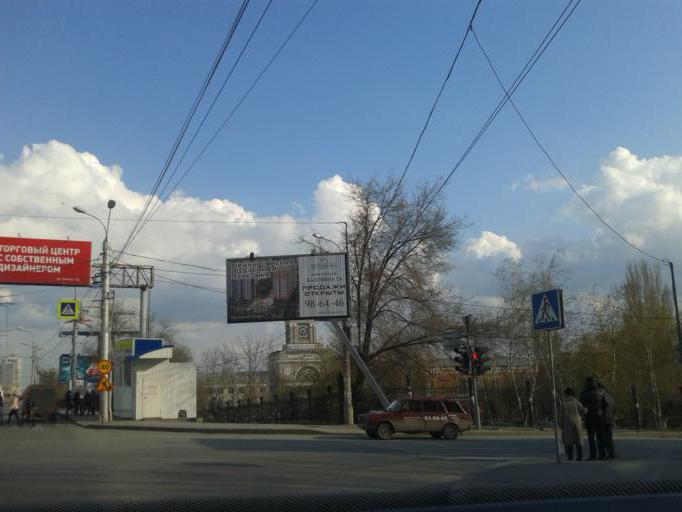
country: RU
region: Volgograd
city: Volgograd
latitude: 48.7150
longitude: 44.5119
